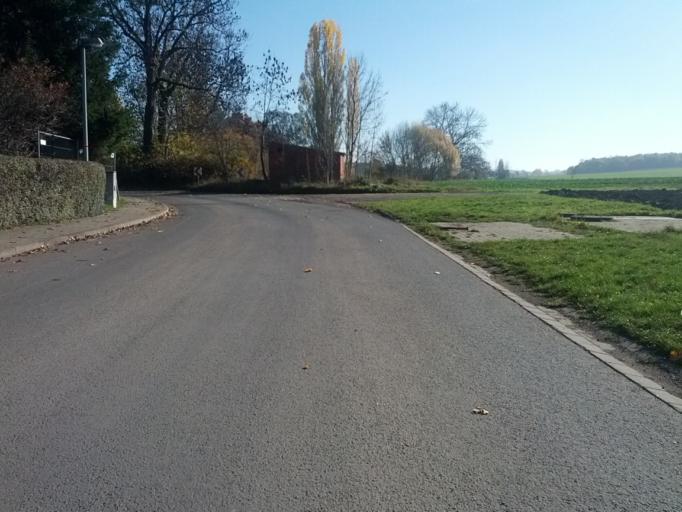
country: DE
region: Thuringia
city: Gotha
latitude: 50.9640
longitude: 10.7007
